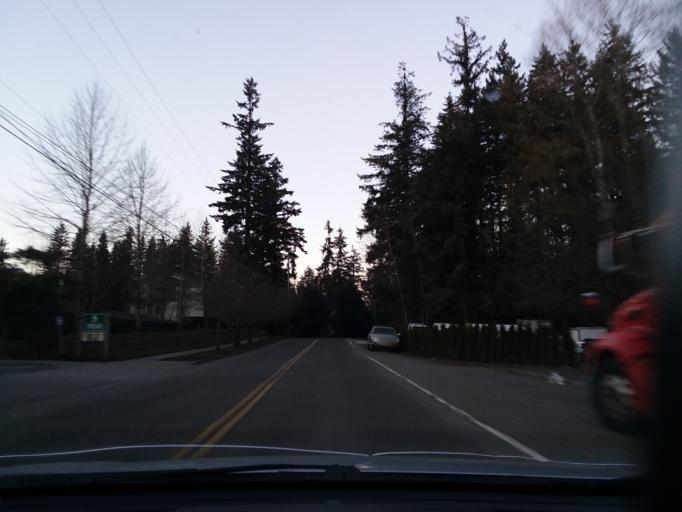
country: US
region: Washington
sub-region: Snohomish County
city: Martha Lake
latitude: 47.8825
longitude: -122.2562
